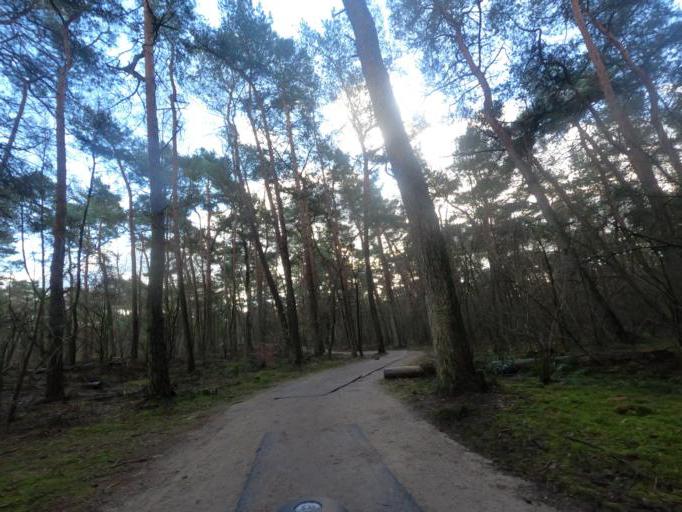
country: NL
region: Utrecht
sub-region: Gemeente Utrechtse Heuvelrug
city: Driebergen-Rijsenburg
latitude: 52.0753
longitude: 5.2753
